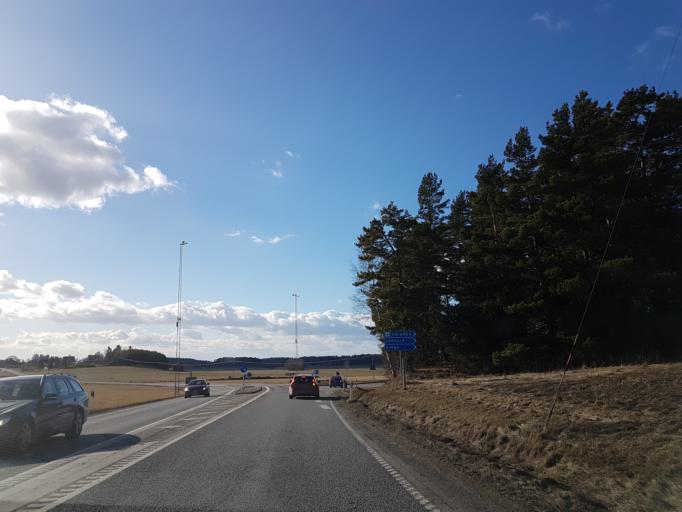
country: SE
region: Stockholm
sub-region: Norrtalje Kommun
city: Rimbo
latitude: 59.7338
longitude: 18.5352
